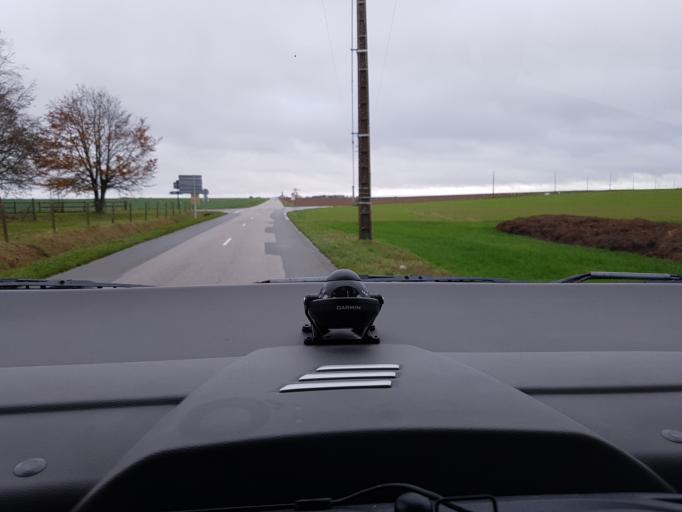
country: FR
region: Haute-Normandie
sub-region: Departement de l'Eure
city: Pont-Saint-Pierre
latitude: 49.3033
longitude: 1.3235
